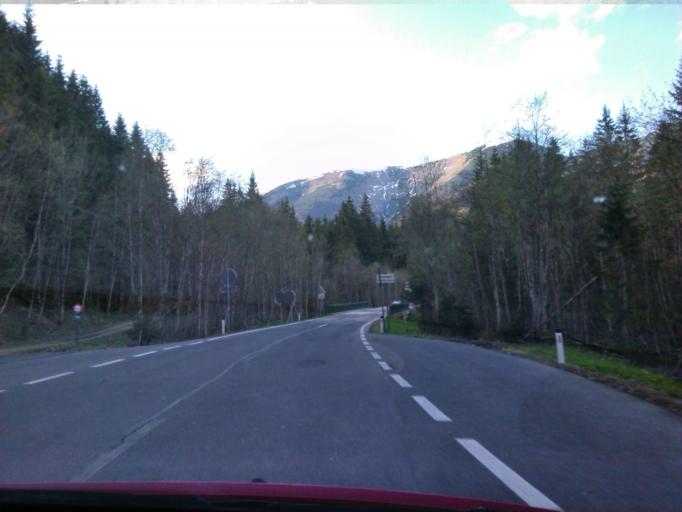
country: AT
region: Styria
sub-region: Politischer Bezirk Bruck-Muerzzuschlag
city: Muerzsteg
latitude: 47.7642
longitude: 15.5132
